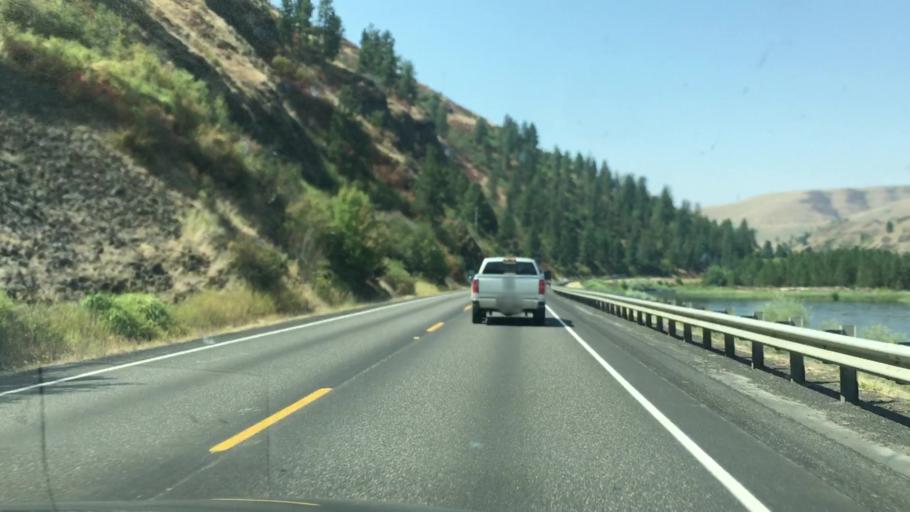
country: US
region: Idaho
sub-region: Nez Perce County
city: Lapwai
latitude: 46.4893
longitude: -116.7322
